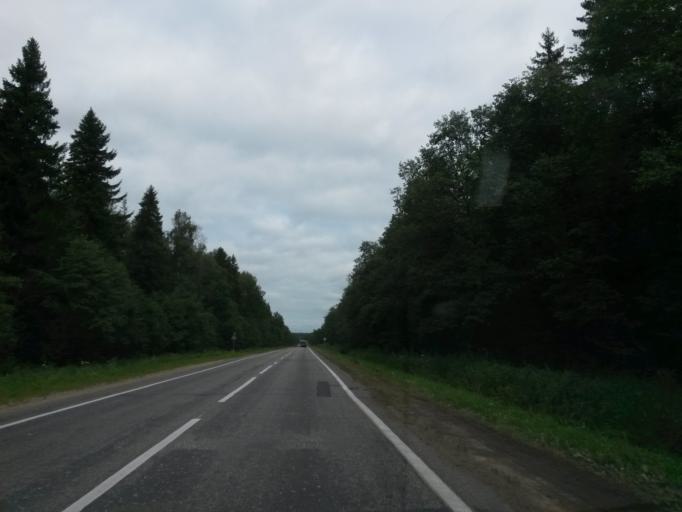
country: RU
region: Jaroslavl
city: Gavrilov-Yam
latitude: 57.4277
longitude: 39.9187
